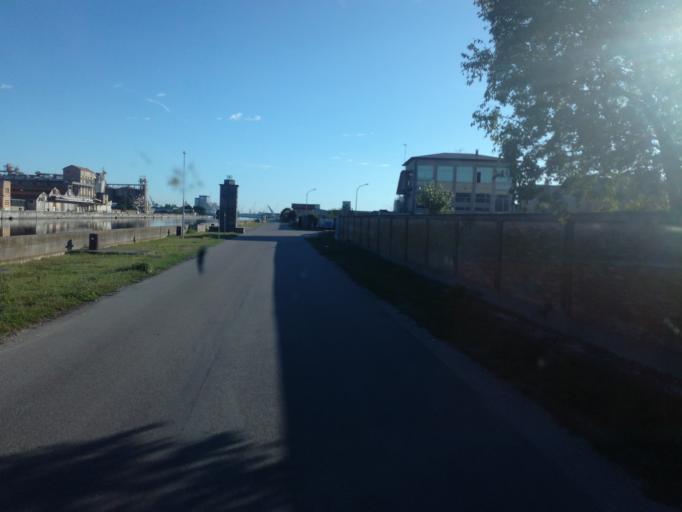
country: IT
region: Emilia-Romagna
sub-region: Provincia di Ravenna
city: Ravenna
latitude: 44.4248
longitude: 12.2188
